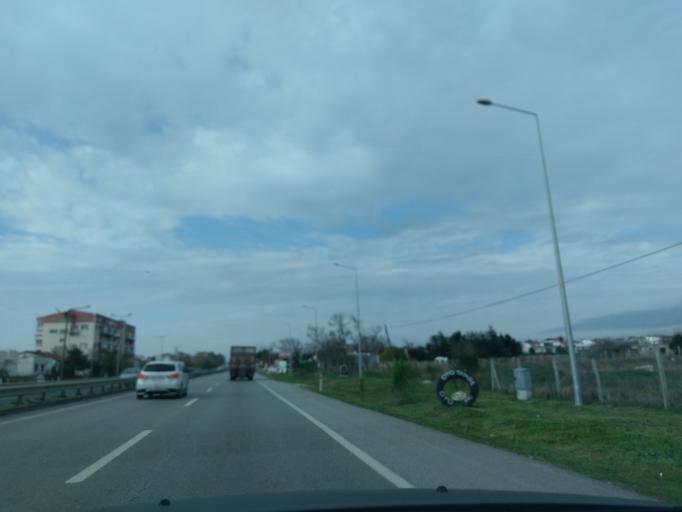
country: TR
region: Istanbul
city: Celaliye
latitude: 41.0474
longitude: 28.4015
